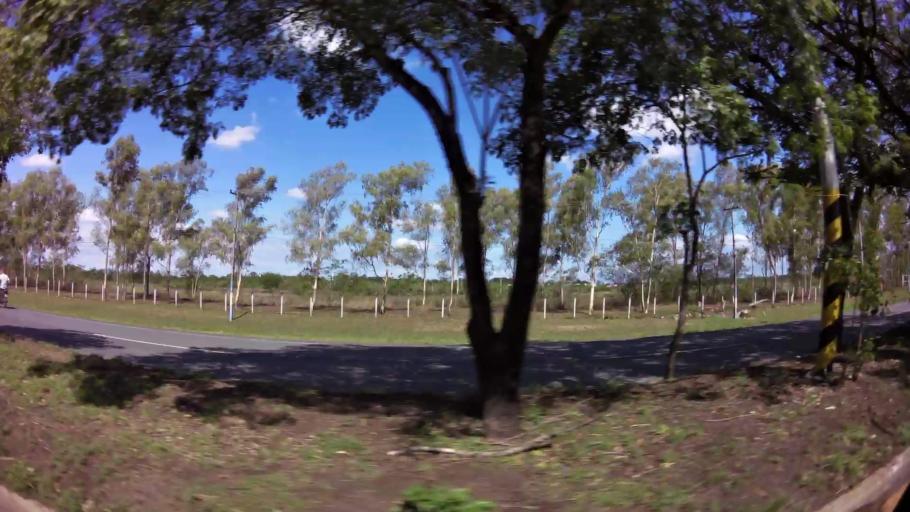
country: PY
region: Central
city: Fernando de la Mora
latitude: -25.2676
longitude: -57.5363
